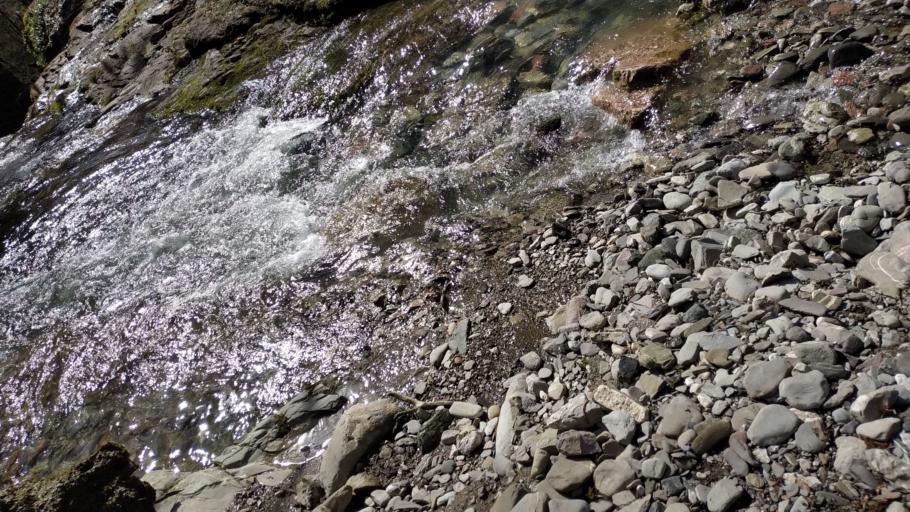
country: RU
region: Krasnodarskiy
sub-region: Sochi City
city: Sochi
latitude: 43.7106
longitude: 39.8191
